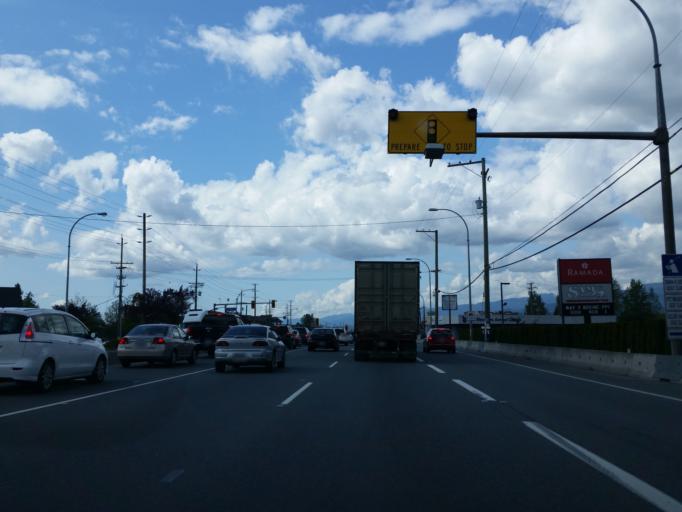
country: CA
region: British Columbia
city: Pitt Meadows
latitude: 49.2305
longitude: -122.6877
